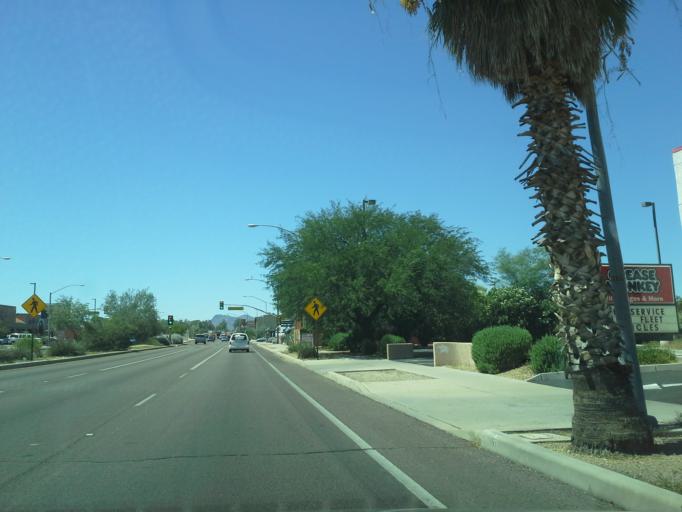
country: US
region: Arizona
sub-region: Pima County
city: Tucson
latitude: 32.2363
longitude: -110.9206
